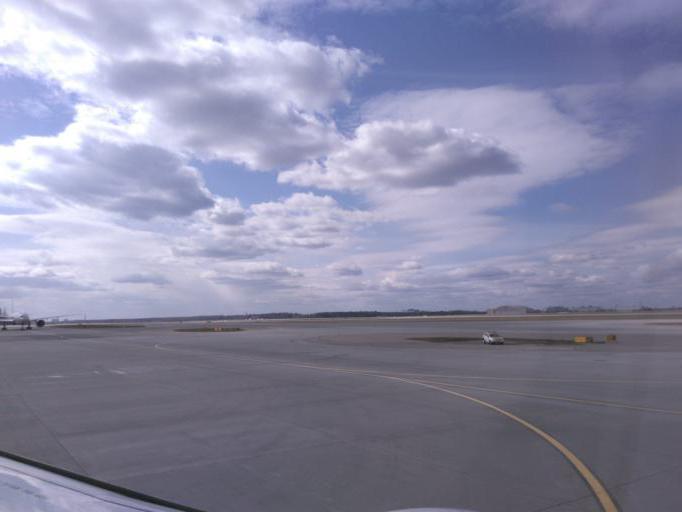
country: RU
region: Moskovskaya
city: Novopodrezkovo
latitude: 55.9674
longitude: 37.4106
